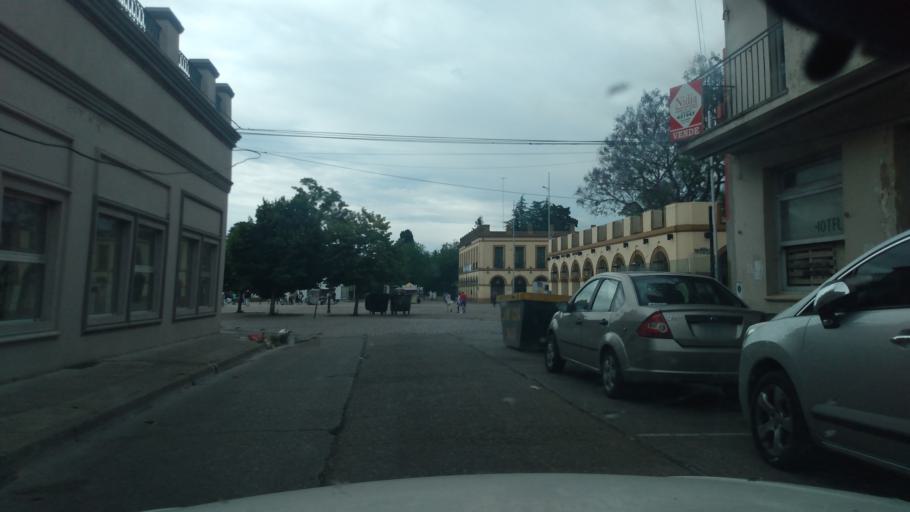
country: AR
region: Buenos Aires
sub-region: Partido de Lujan
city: Lujan
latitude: -34.5630
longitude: -59.1199
